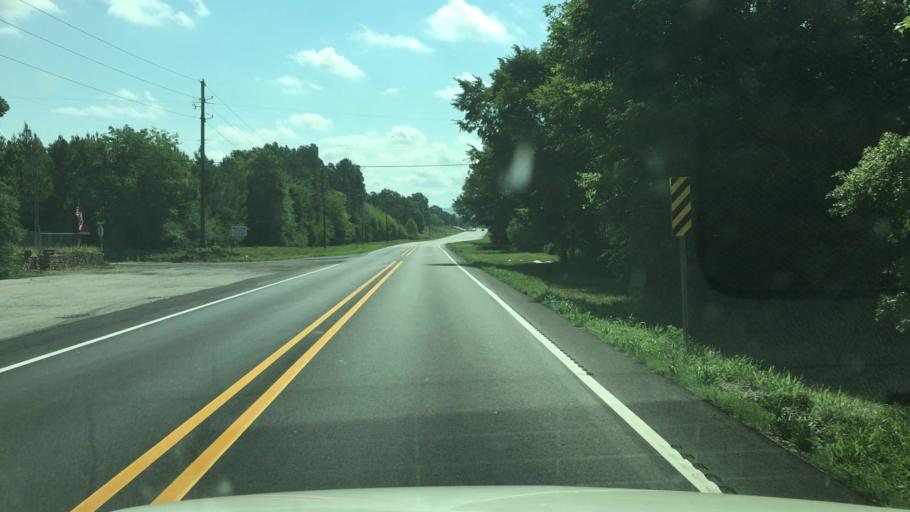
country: US
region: Arkansas
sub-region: Garland County
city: Piney
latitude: 34.5115
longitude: -93.2415
